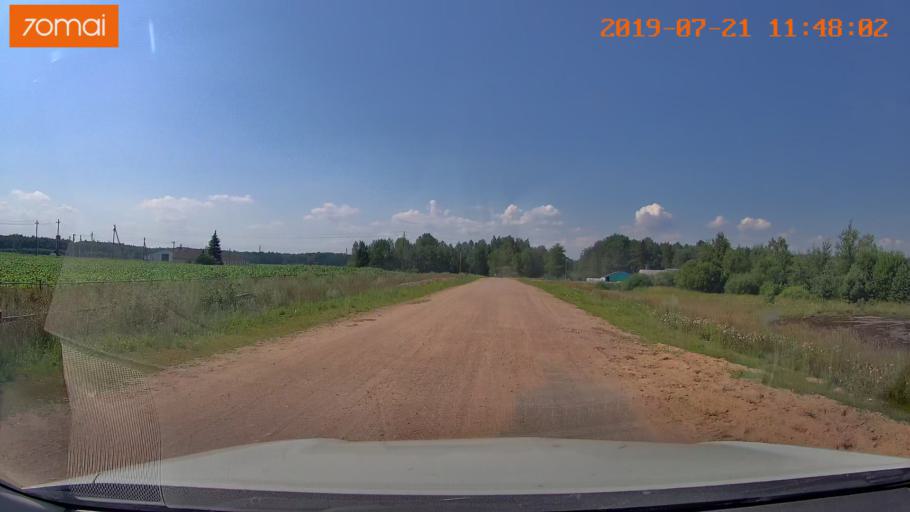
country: BY
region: Grodnenskaya
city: Lyubcha
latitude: 53.8999
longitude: 26.0550
